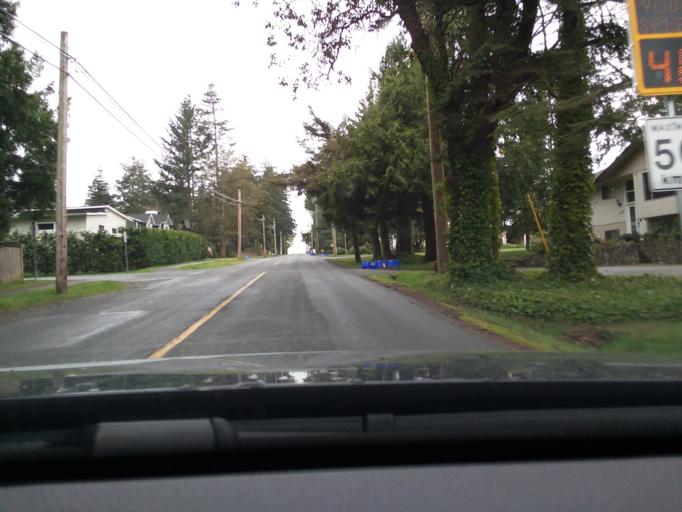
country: CA
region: British Columbia
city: North Saanich
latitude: 48.5544
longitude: -123.3968
